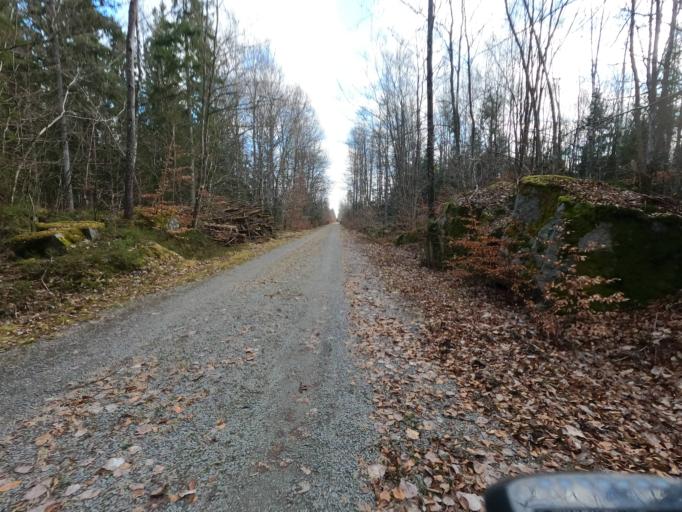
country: SE
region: Kronoberg
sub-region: Vaxjo Kommun
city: Gemla
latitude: 56.6588
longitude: 14.6190
